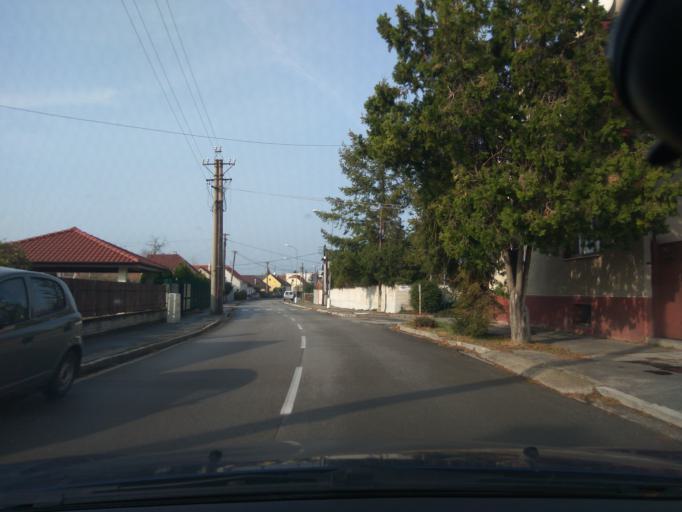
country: SK
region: Trnavsky
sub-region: Okres Trnava
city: Piestany
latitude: 48.6048
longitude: 17.8269
